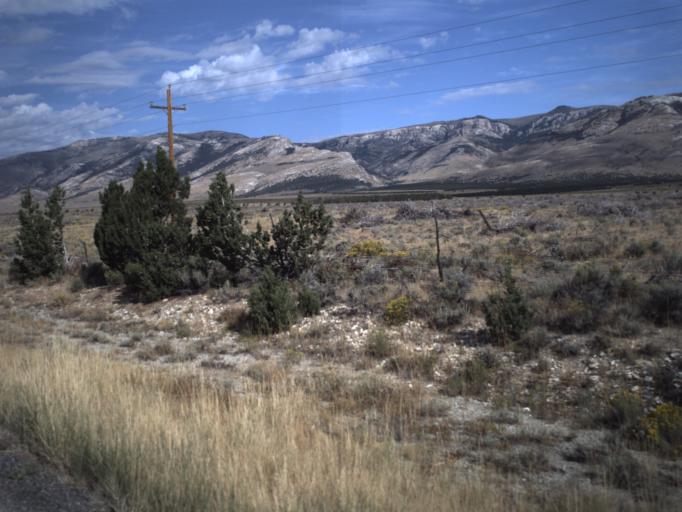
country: US
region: Idaho
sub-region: Cassia County
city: Burley
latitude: 41.8168
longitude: -113.3911
